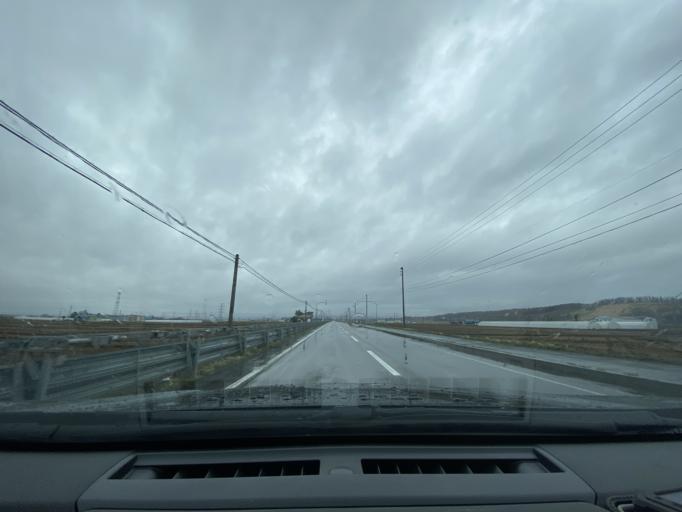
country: JP
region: Hokkaido
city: Fukagawa
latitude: 43.8148
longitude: 141.9761
